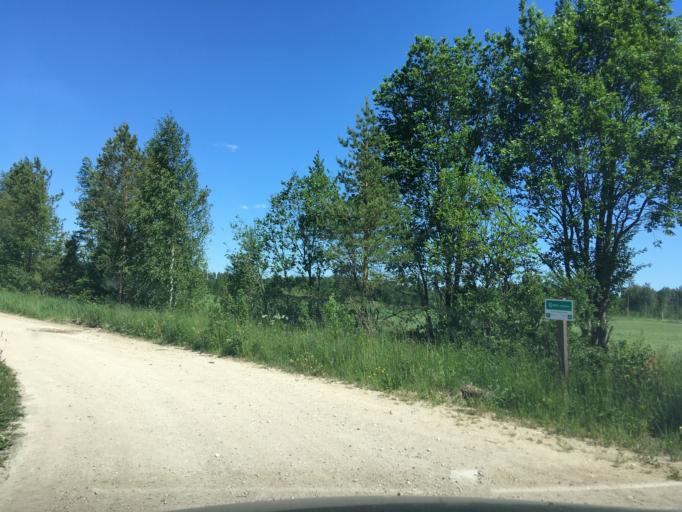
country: EE
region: Harju
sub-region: Raasiku vald
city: Raasiku
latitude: 59.1568
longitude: 25.1598
